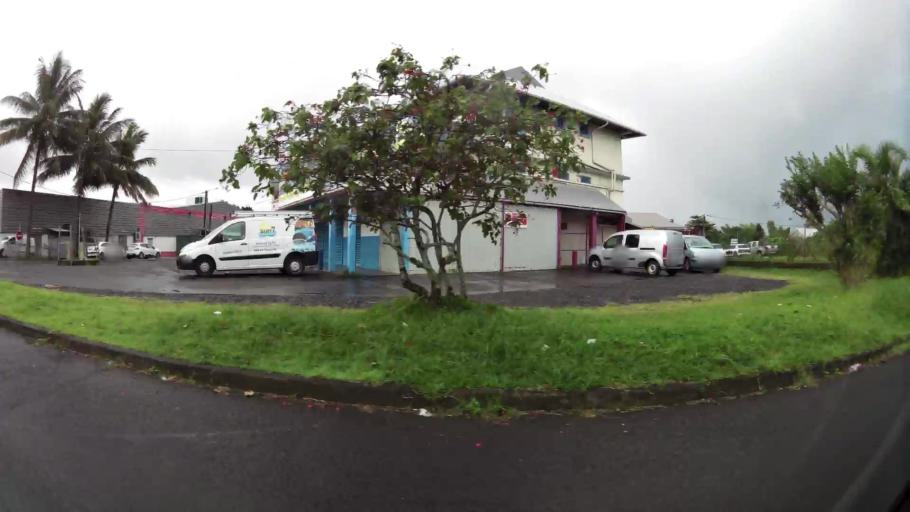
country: RE
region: Reunion
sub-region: Reunion
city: Saint-Andre
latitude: -20.9312
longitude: 55.6390
